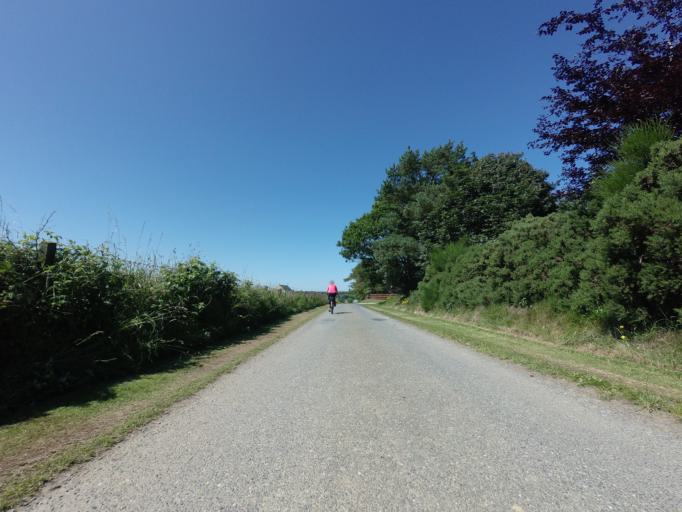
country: GB
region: Scotland
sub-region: Aberdeenshire
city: Macduff
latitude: 57.6390
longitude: -2.4966
